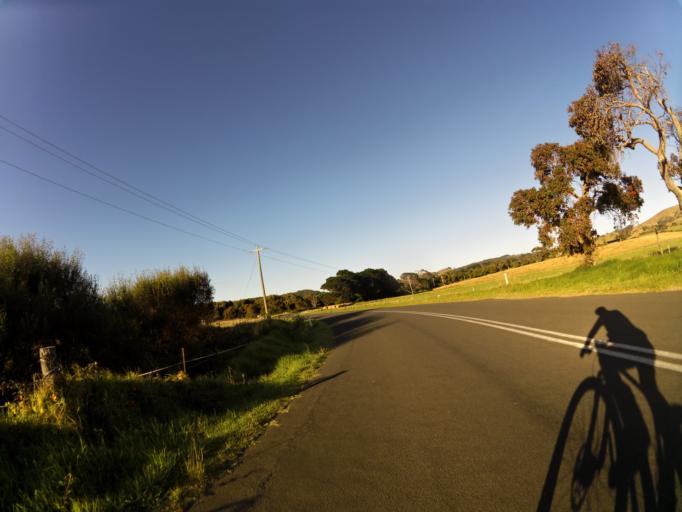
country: AU
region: Victoria
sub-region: Colac-Otway
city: Apollo Bay
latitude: -38.7665
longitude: 143.6589
